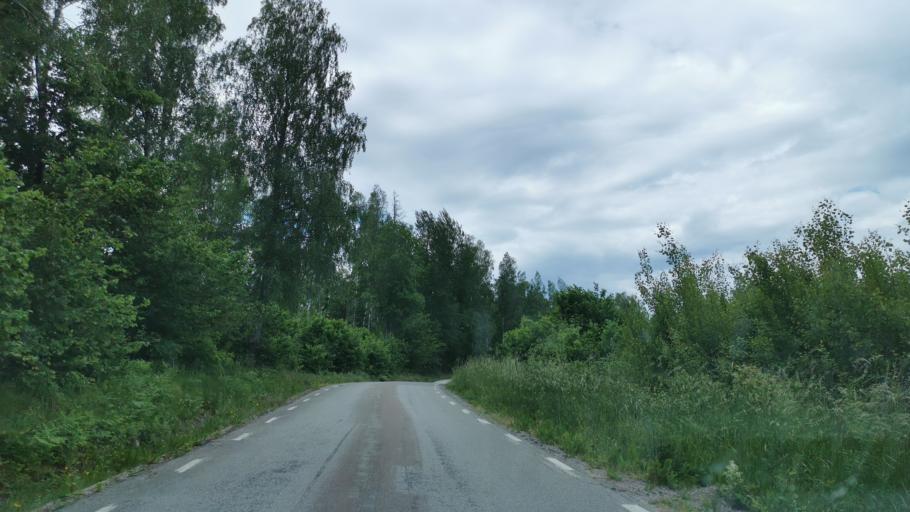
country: SE
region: Vaestra Goetaland
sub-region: Bengtsfors Kommun
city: Dals Langed
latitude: 58.8475
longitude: 12.4077
